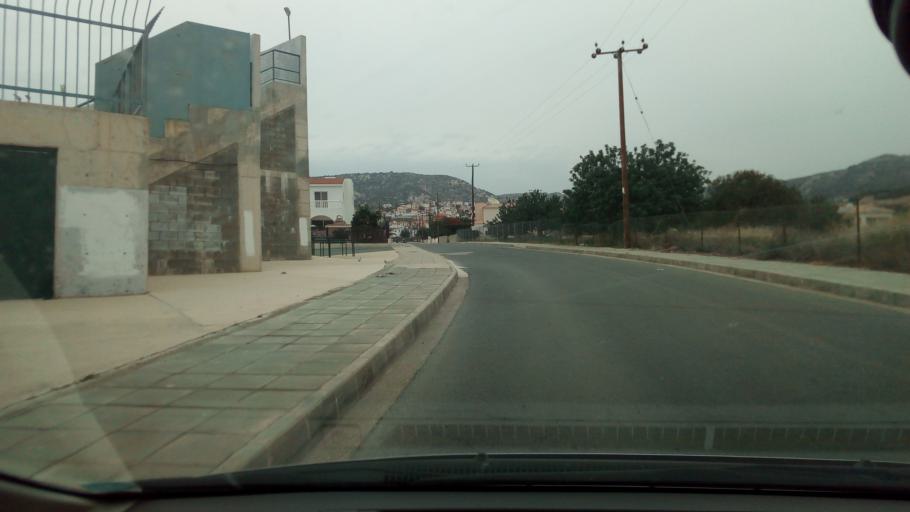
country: CY
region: Pafos
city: Pegeia
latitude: 34.8750
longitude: 32.3833
